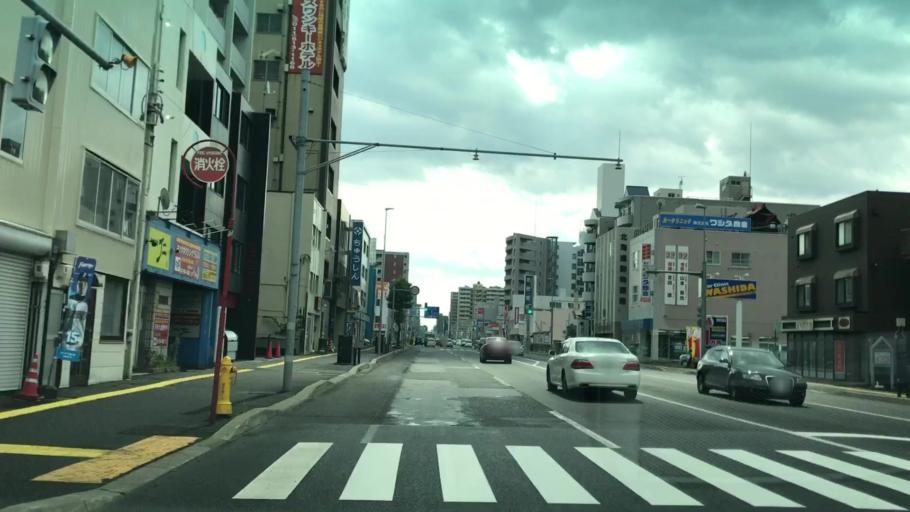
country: JP
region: Hokkaido
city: Sapporo
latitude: 43.0533
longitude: 141.3684
